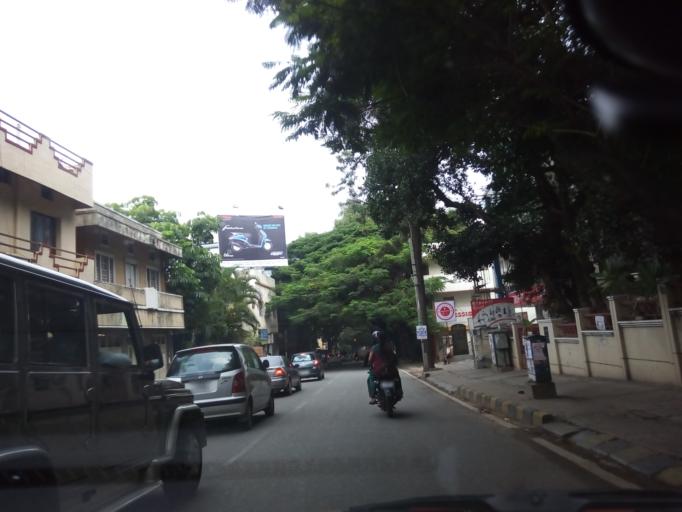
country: IN
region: Karnataka
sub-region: Bangalore Urban
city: Bangalore
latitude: 13.0073
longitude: 77.5692
